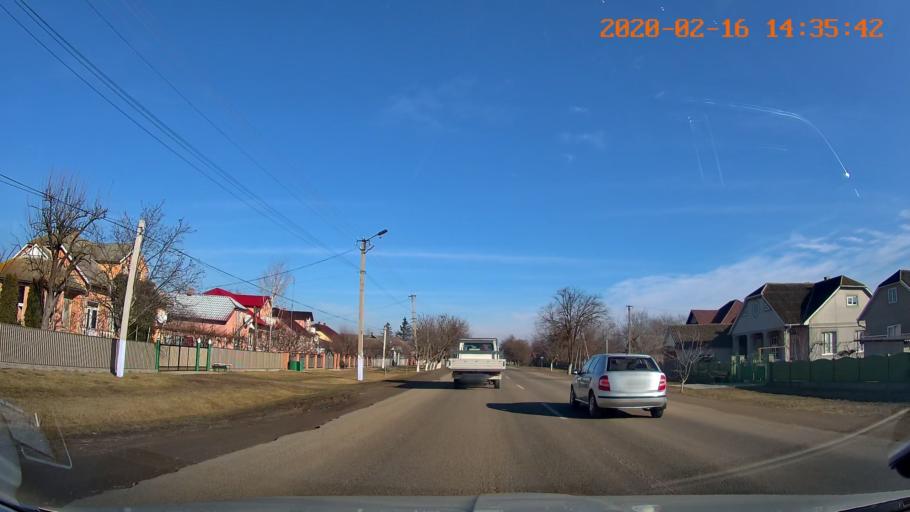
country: RO
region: Botosani
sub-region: Comuna Darabani
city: Bajura
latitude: 48.2234
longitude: 26.4958
